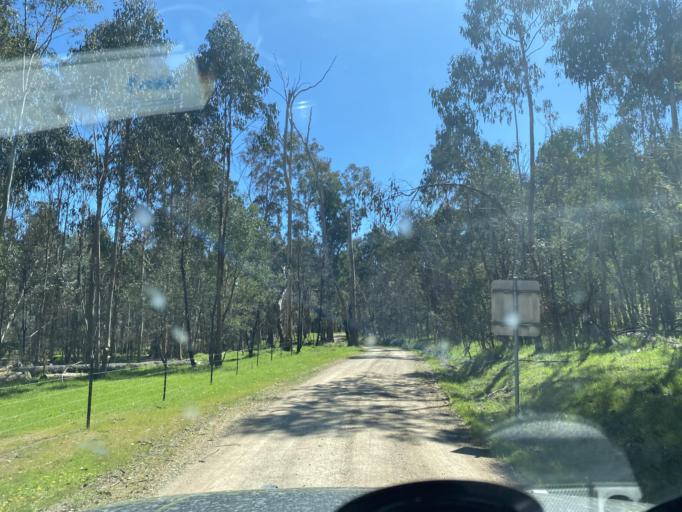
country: AU
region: Victoria
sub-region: Benalla
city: Benalla
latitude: -36.6979
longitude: 146.1777
